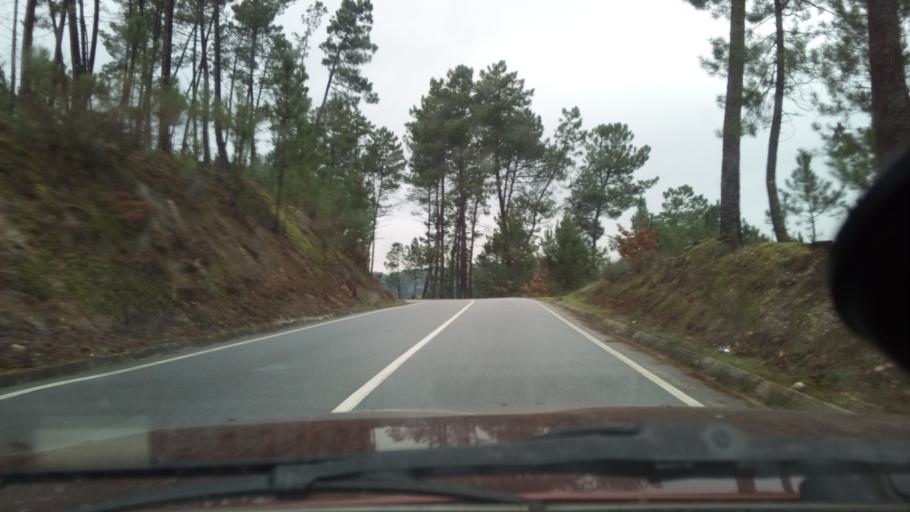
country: PT
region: Viseu
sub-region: Mangualde
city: Mangualde
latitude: 40.6151
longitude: -7.8036
